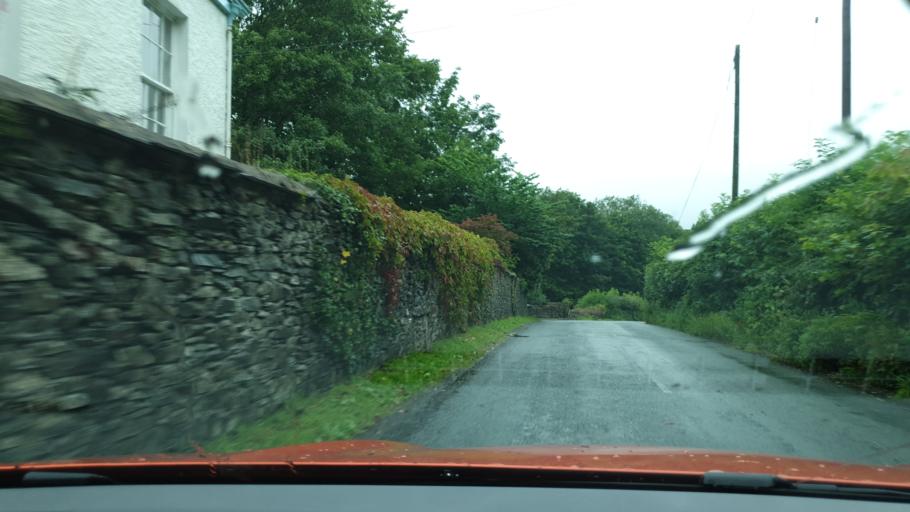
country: GB
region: England
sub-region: Cumbria
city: Ulverston
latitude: 54.2533
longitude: -3.0631
